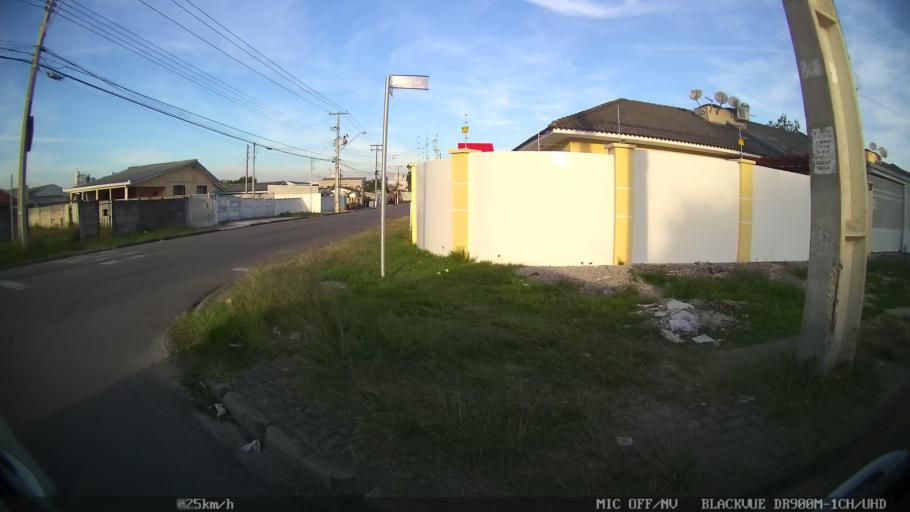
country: BR
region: Parana
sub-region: Pinhais
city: Pinhais
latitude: -25.4466
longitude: -49.1737
